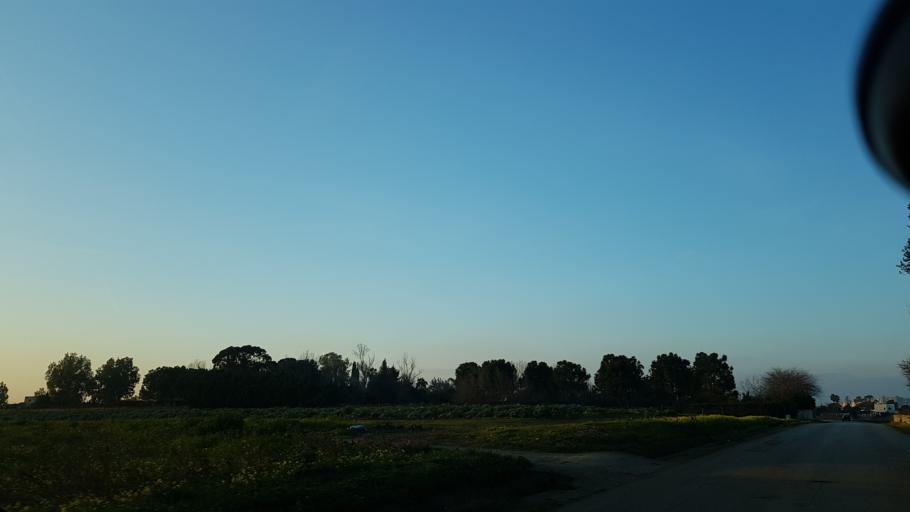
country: IT
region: Apulia
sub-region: Provincia di Brindisi
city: La Rosa
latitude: 40.6026
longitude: 17.9462
